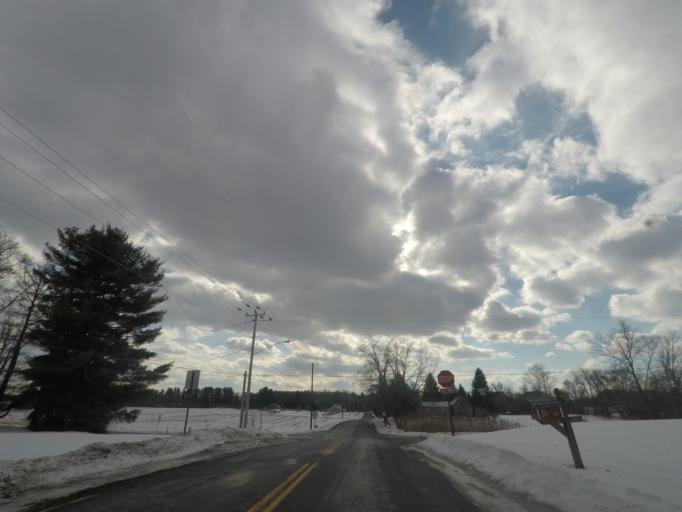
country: US
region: New York
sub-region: Saratoga County
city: Mechanicville
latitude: 42.9039
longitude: -73.7457
